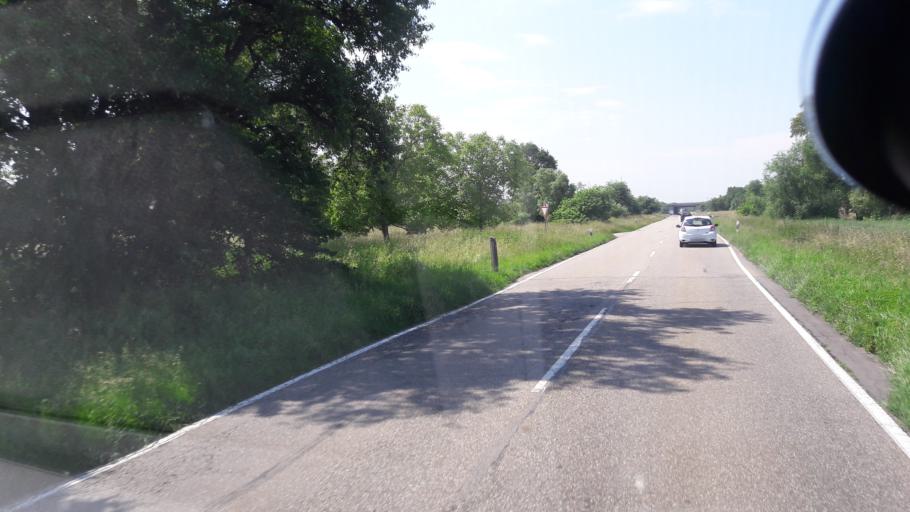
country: DE
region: Baden-Wuerttemberg
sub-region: Karlsruhe Region
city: Muggensturm
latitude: 48.8571
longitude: 8.2700
